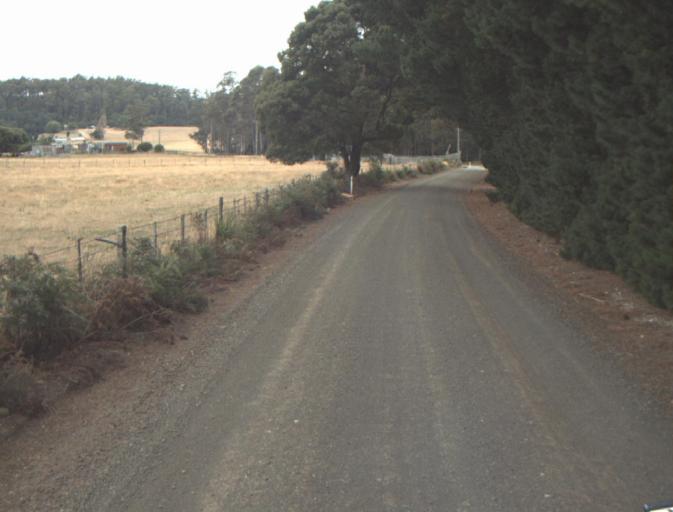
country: AU
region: Tasmania
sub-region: Launceston
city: Mayfield
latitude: -41.2089
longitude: 147.1860
